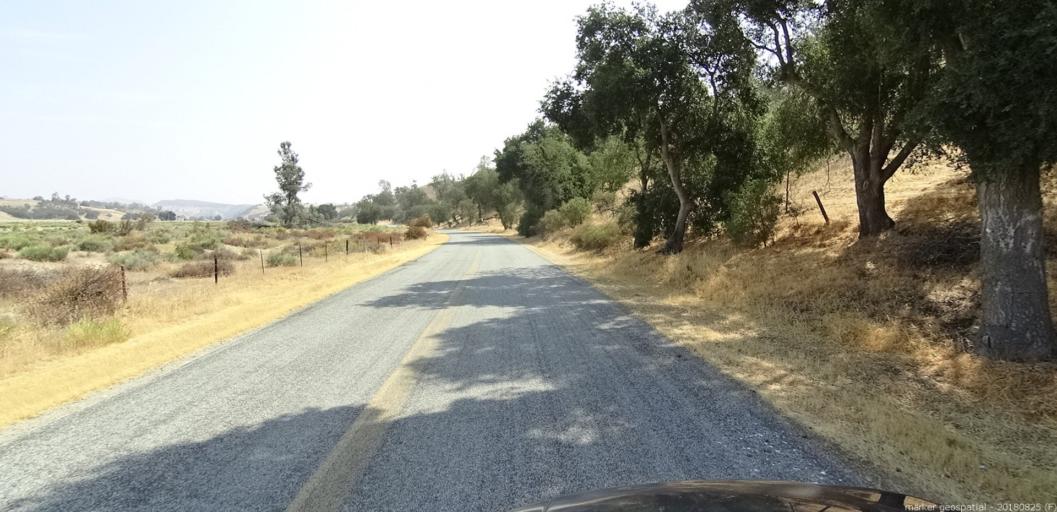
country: US
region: California
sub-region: San Luis Obispo County
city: San Miguel
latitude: 35.8368
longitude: -120.6264
